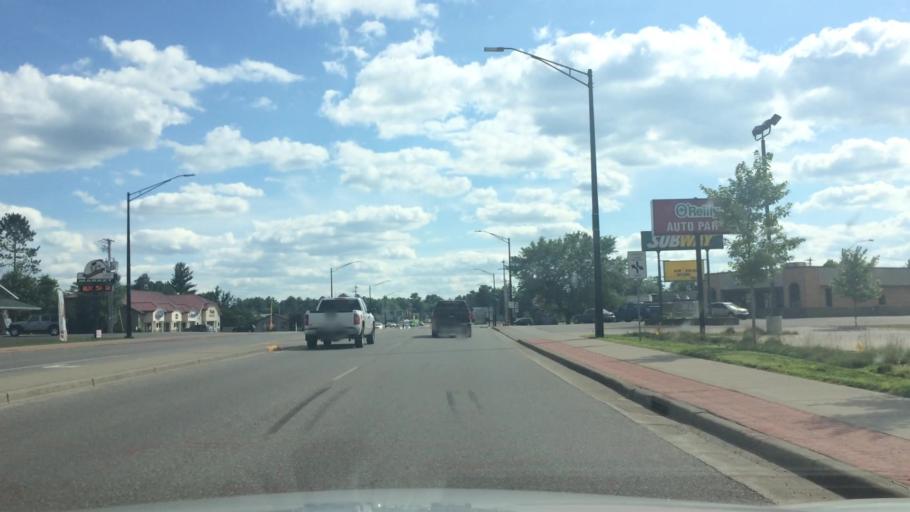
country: US
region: Wisconsin
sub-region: Vilas County
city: Lac du Flambeau
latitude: 45.8903
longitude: -89.7016
